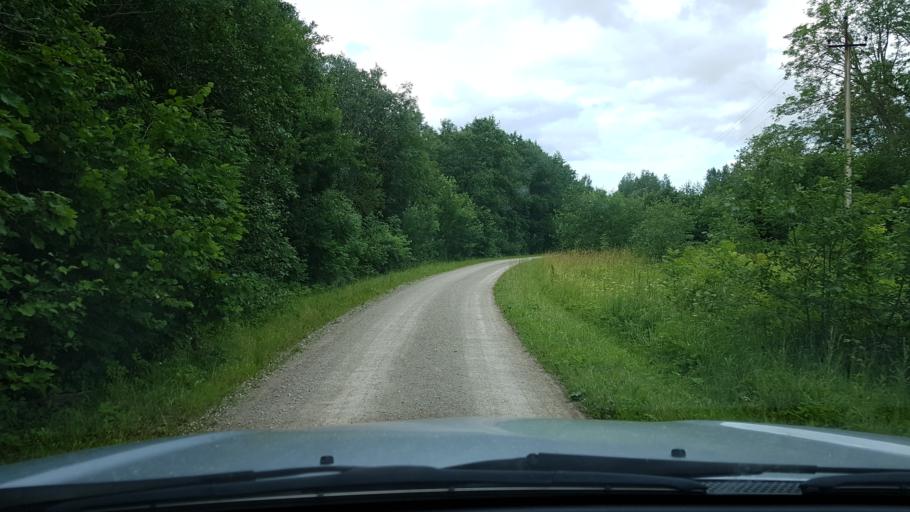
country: EE
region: Ida-Virumaa
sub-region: Narva-Joesuu linn
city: Narva-Joesuu
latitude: 59.4080
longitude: 27.9812
